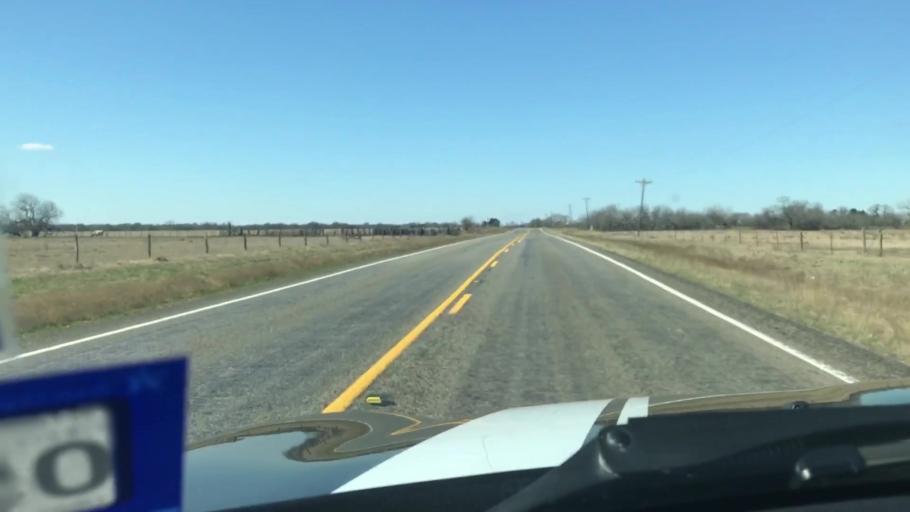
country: US
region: Texas
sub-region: Robertson County
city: Calvert
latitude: 30.8854
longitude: -96.8011
